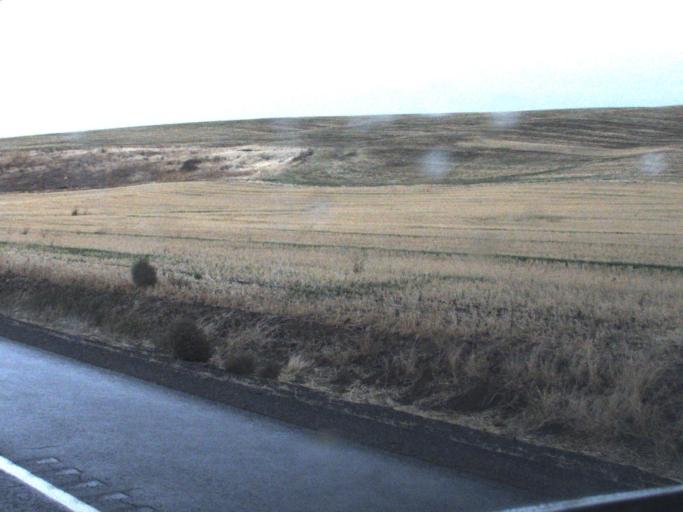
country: US
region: Washington
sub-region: Whitman County
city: Colfax
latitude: 46.8344
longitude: -117.3331
